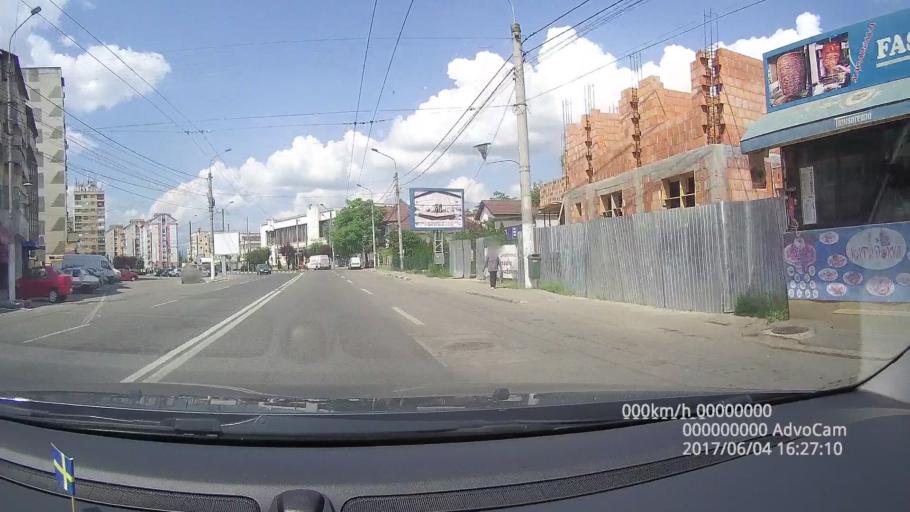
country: RO
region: Gorj
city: Targu Jiu
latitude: 45.0320
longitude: 23.2791
